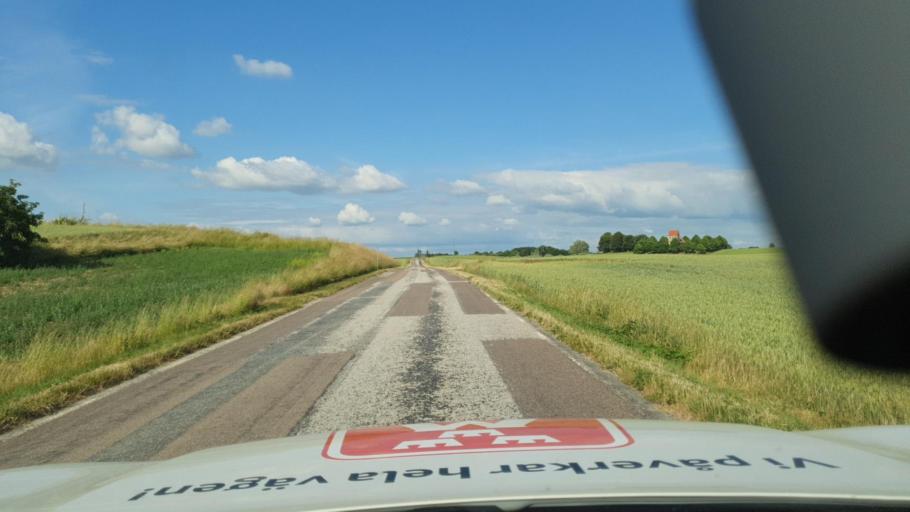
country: SE
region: Skane
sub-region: Skurups Kommun
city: Rydsgard
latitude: 55.4386
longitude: 13.6255
